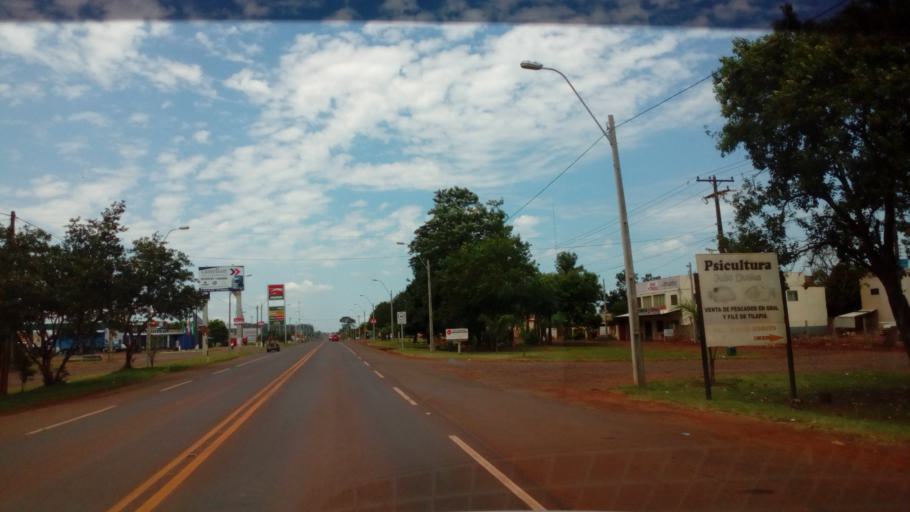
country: PY
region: Alto Parana
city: Santa Rita
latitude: -25.7516
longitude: -55.0570
